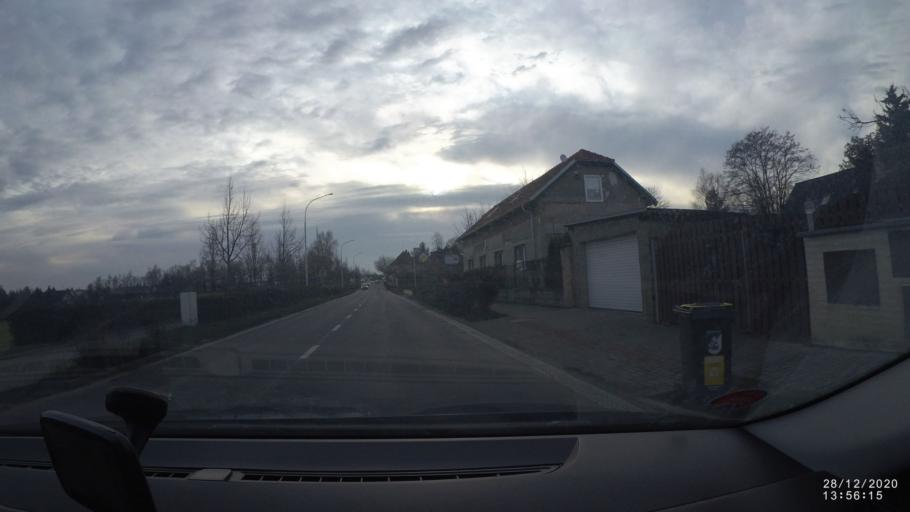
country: CZ
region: Central Bohemia
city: Sestajovice
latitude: 50.1078
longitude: 14.6812
